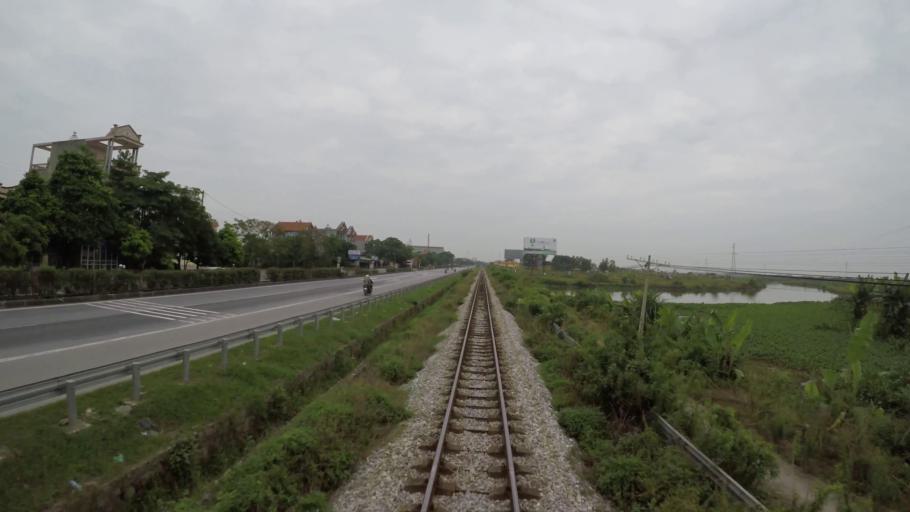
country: VN
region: Hai Duong
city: Phu Thai
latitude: 20.9455
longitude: 106.5409
